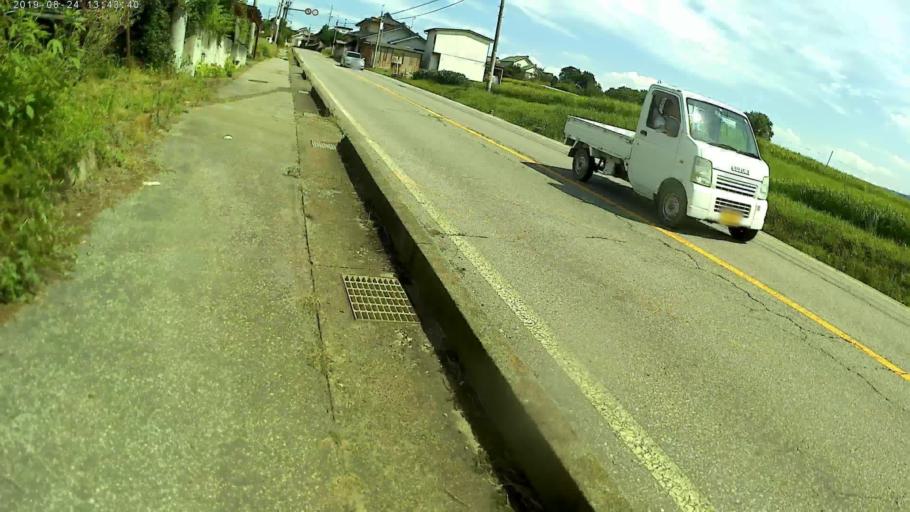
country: JP
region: Nagano
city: Komoro
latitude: 36.2753
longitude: 138.4017
